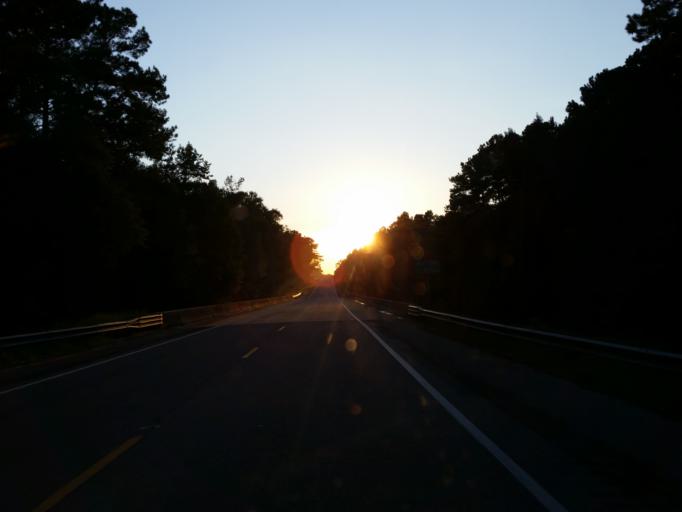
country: US
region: Georgia
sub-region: Berrien County
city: Nashville
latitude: 31.2159
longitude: -83.2728
